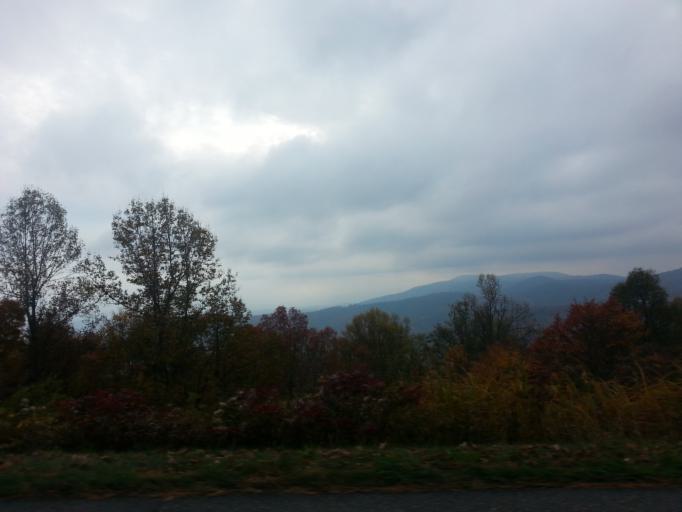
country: US
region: North Carolina
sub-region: Ashe County
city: West Jefferson
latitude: 36.2810
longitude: -81.3863
